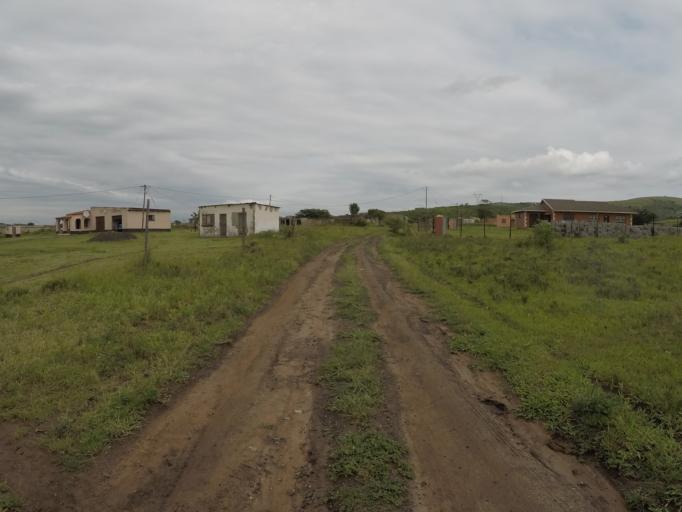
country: ZA
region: KwaZulu-Natal
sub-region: uThungulu District Municipality
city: Empangeni
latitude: -28.7113
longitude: 31.8636
